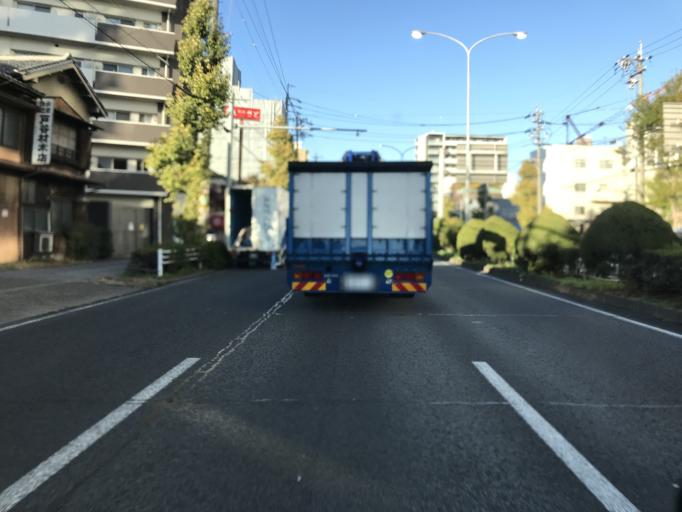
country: JP
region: Aichi
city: Nagoya-shi
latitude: 35.1687
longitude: 136.8725
